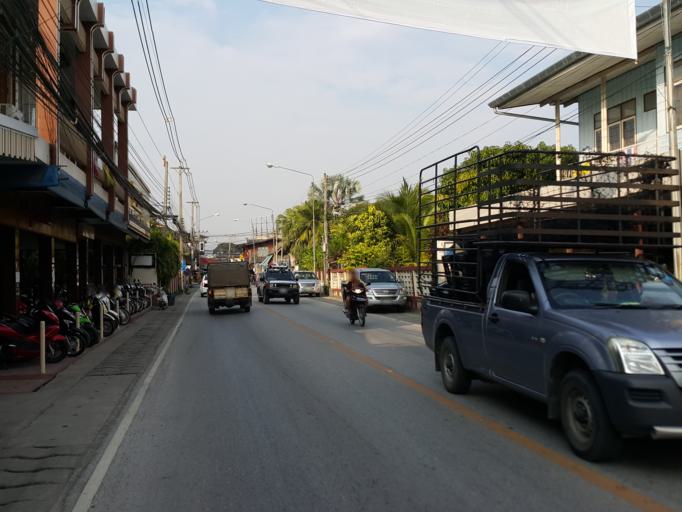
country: TH
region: Chiang Mai
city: San Sai
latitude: 18.8719
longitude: 99.1363
